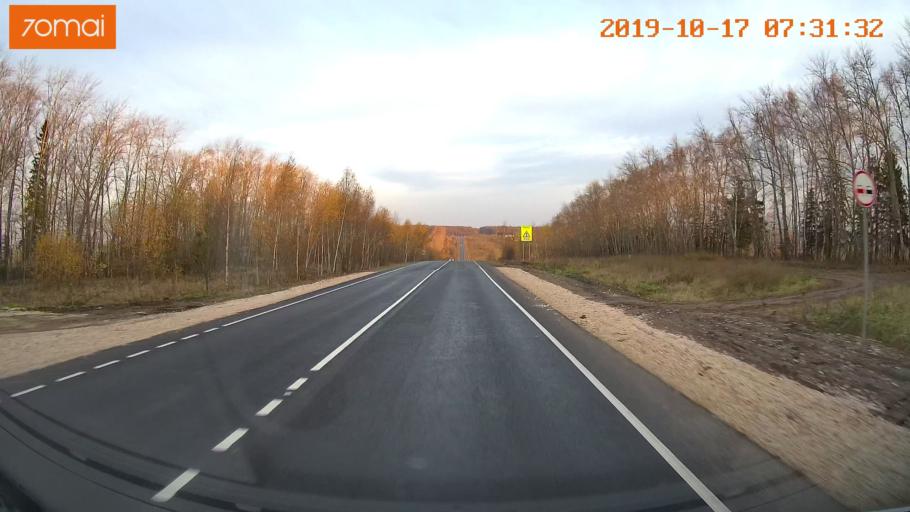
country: RU
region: Ivanovo
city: Gavrilov Posad
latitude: 56.3904
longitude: 39.9941
